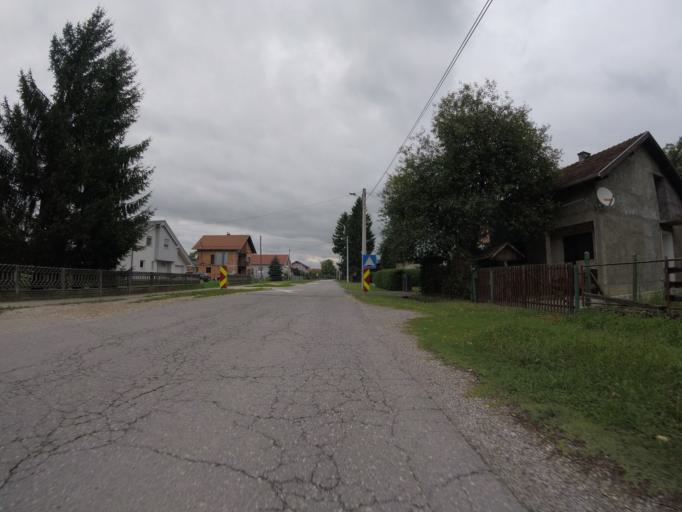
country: HR
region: Zagrebacka
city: Turopolje
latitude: 45.6537
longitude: 16.1408
